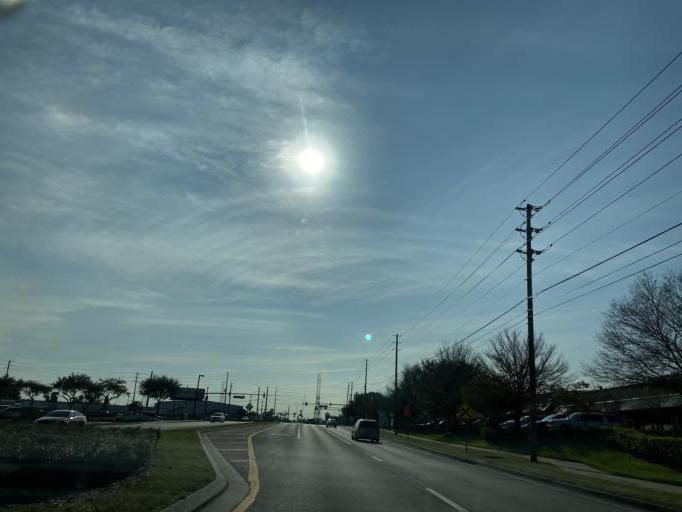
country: US
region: Florida
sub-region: Seminole County
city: Longwood
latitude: 28.7230
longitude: -81.3350
